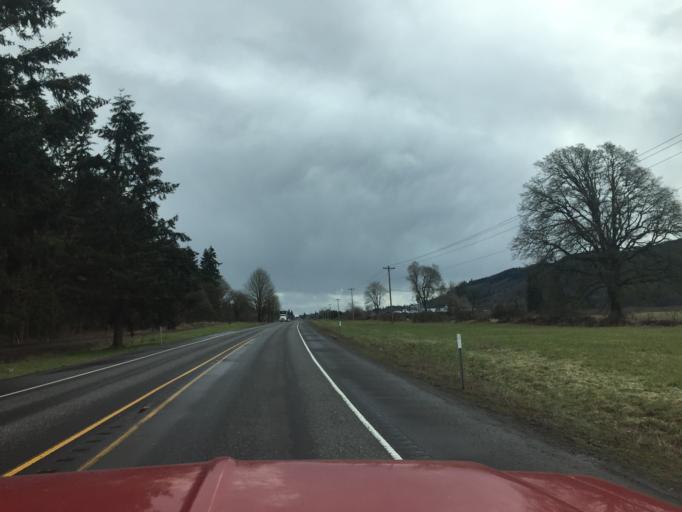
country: US
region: Oregon
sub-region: Columbia County
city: Columbia City
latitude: 45.9242
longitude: -122.8357
